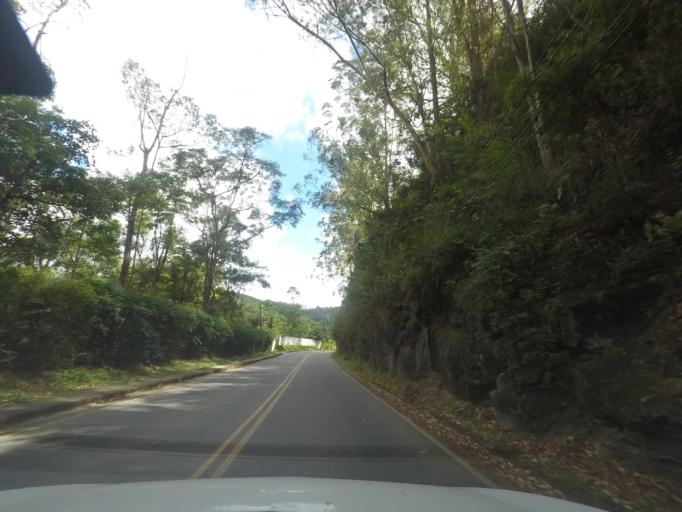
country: BR
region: Rio de Janeiro
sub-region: Teresopolis
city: Teresopolis
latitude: -22.3967
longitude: -42.9913
